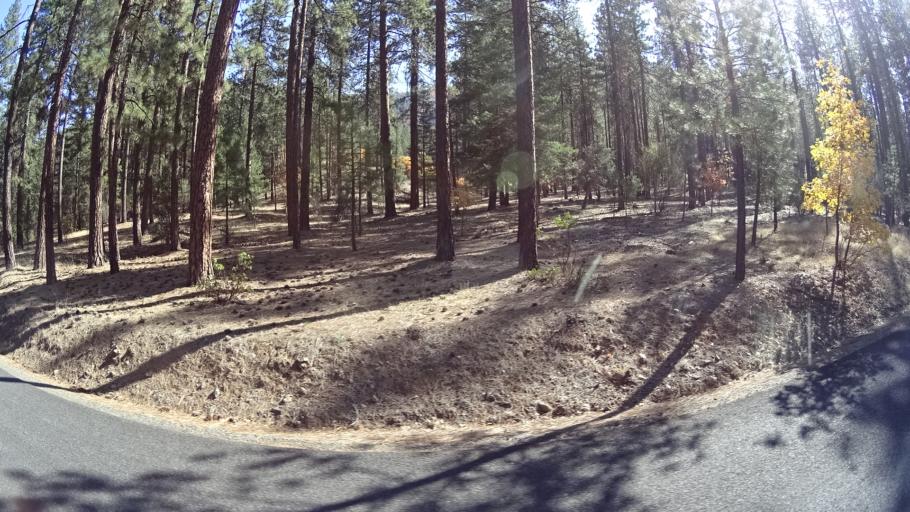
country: US
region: California
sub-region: Siskiyou County
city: Yreka
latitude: 41.6520
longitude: -122.8632
